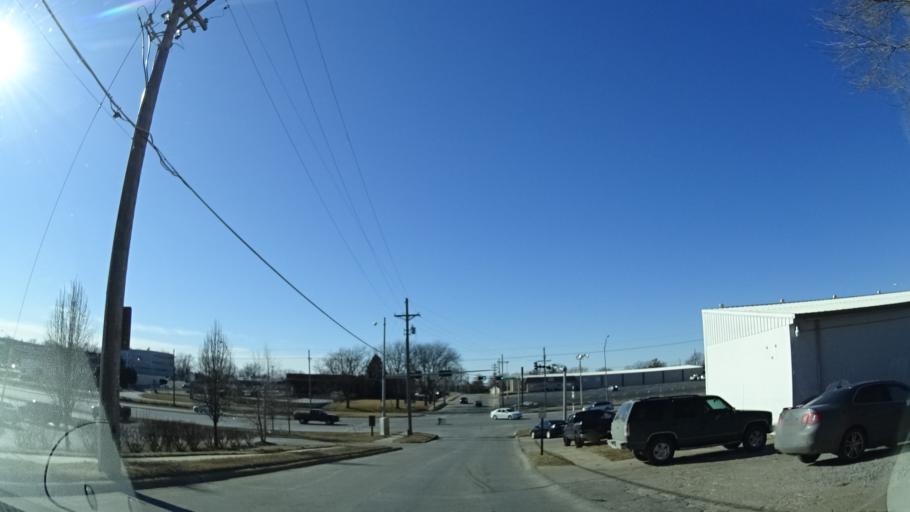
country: US
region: Nebraska
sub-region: Sarpy County
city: Offutt Air Force Base
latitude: 41.1476
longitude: -95.9266
